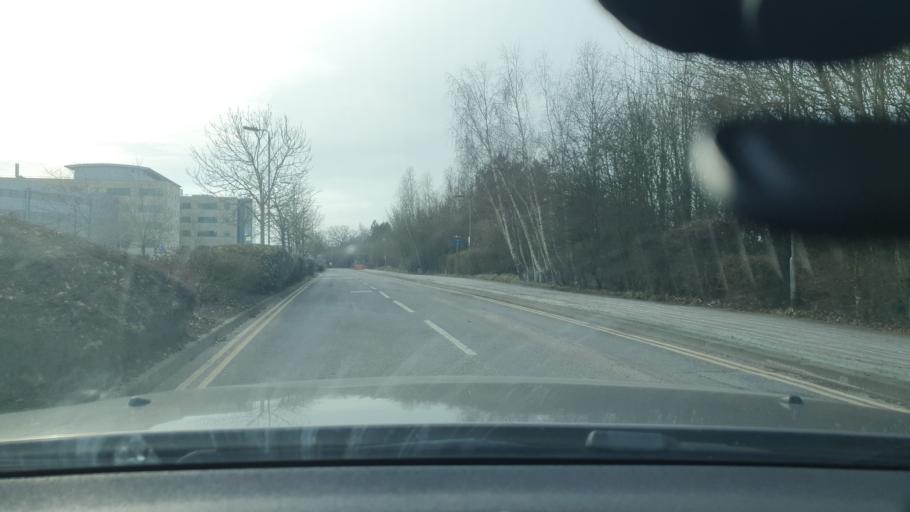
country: GB
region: England
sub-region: Borough of Swindon
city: Chiseldon
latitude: 51.5397
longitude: -1.7295
